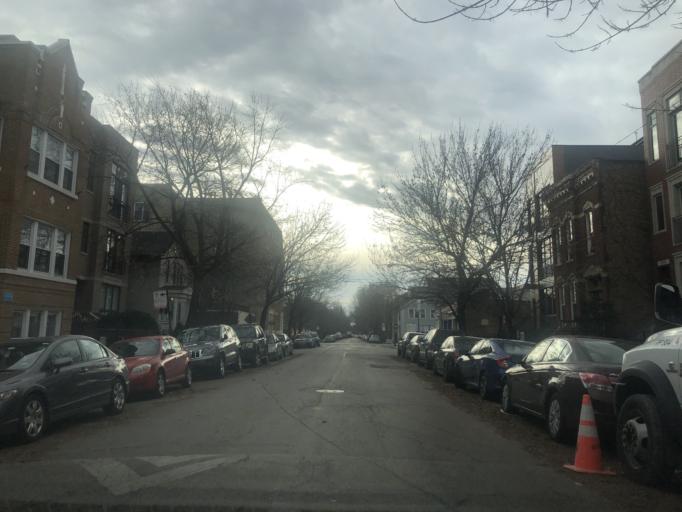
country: US
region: Illinois
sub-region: Cook County
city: Chicago
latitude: 41.9006
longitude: -87.6699
